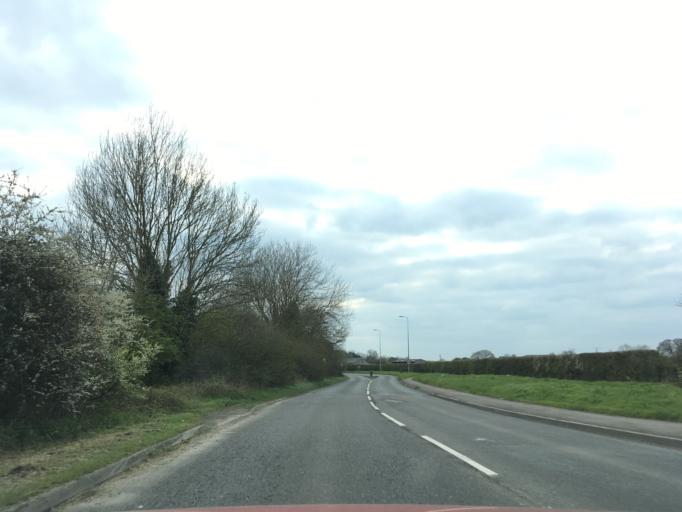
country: GB
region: England
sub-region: Oxfordshire
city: North Leigh
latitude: 51.7983
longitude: -1.4626
